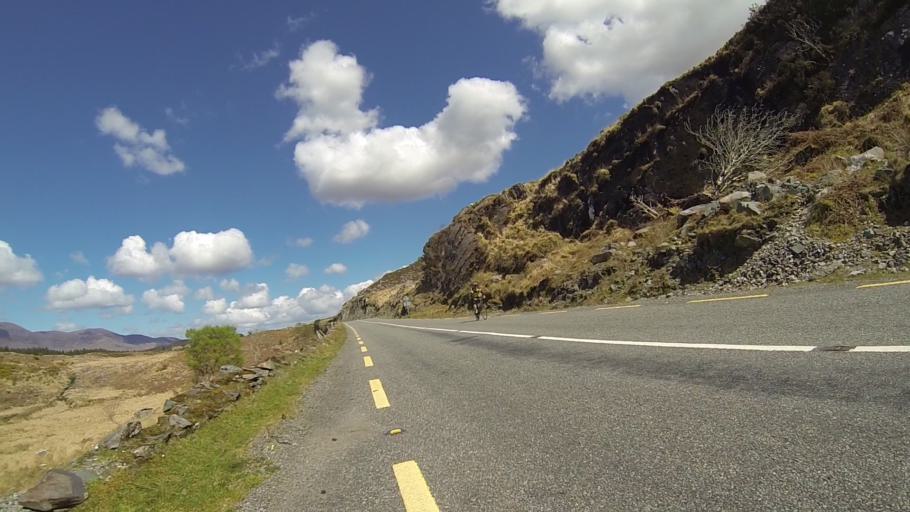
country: IE
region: Munster
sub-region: Ciarrai
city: Kenmare
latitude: 51.9481
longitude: -9.6307
